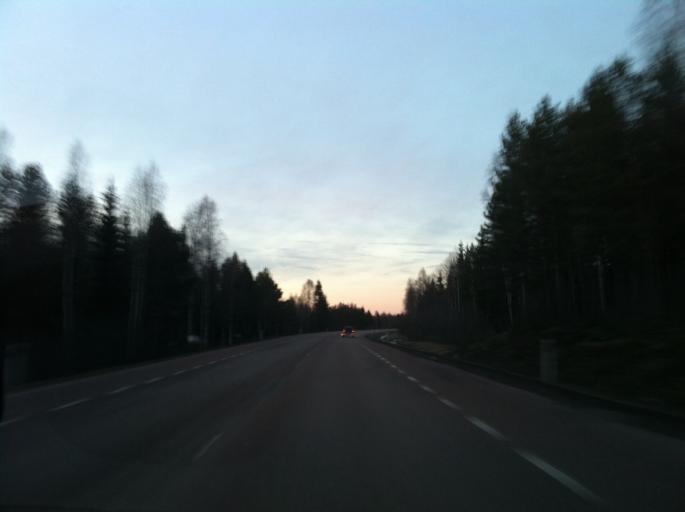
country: SE
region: Dalarna
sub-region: Orsa Kommun
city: Orsa
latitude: 61.0536
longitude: 14.6101
